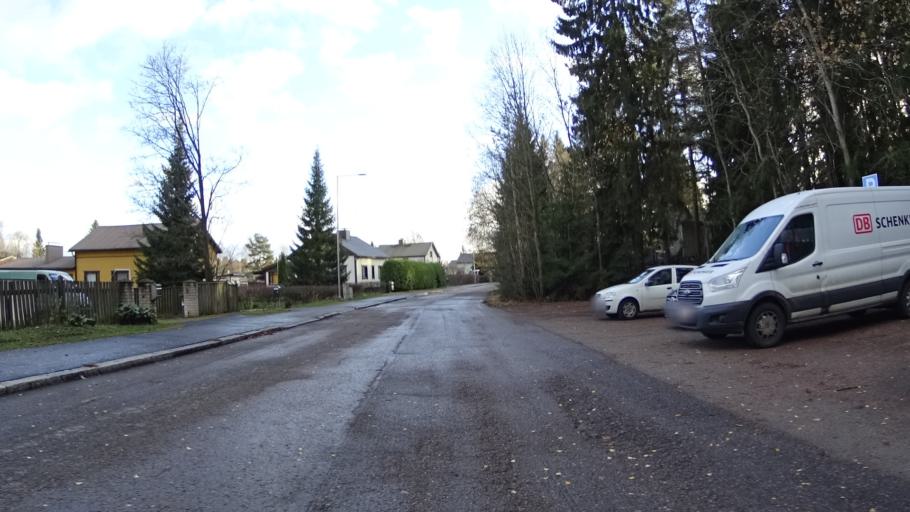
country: FI
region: Uusimaa
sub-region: Helsinki
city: Vantaa
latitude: 60.3054
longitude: 25.0296
